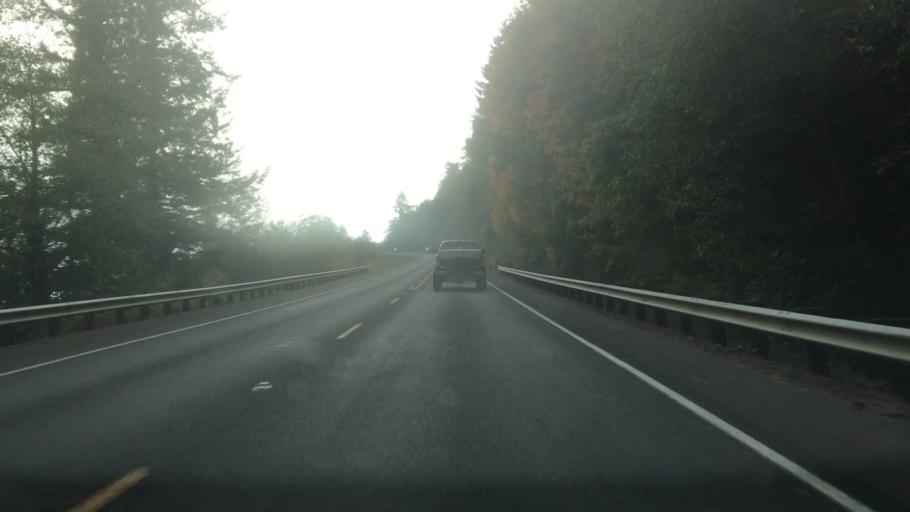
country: US
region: Oregon
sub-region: Clatsop County
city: Astoria
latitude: 46.2759
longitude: -123.8154
